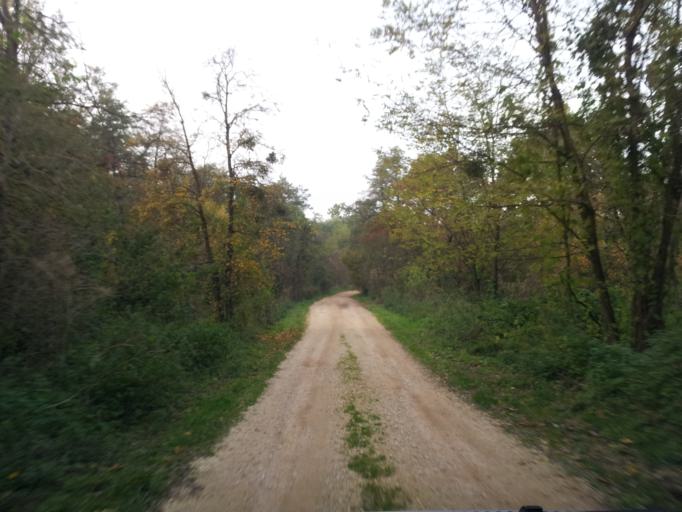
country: HU
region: Gyor-Moson-Sopron
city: Bakonyszentlaszlo
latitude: 47.3689
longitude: 17.8177
